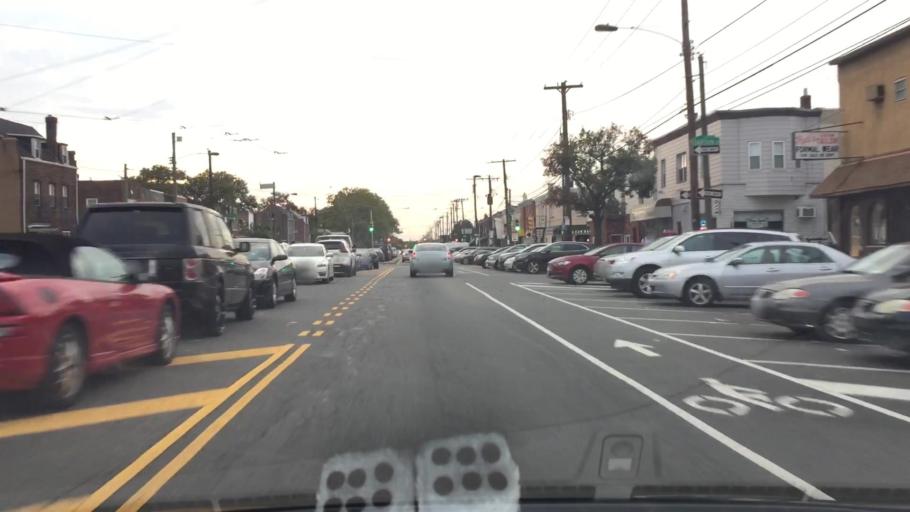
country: US
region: Pennsylvania
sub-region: Philadelphia County
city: Philadelphia
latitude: 39.9163
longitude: -75.1667
